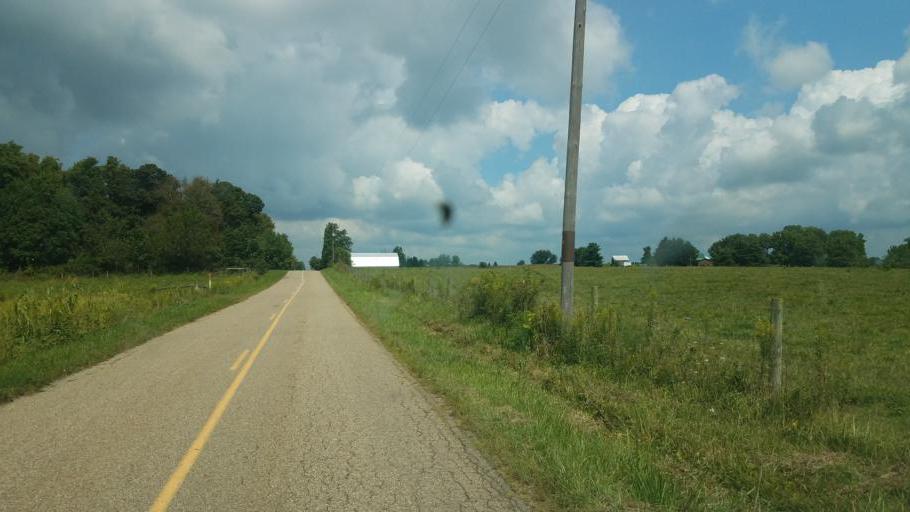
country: US
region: Ohio
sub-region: Licking County
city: Utica
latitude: 40.2825
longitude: -82.4900
